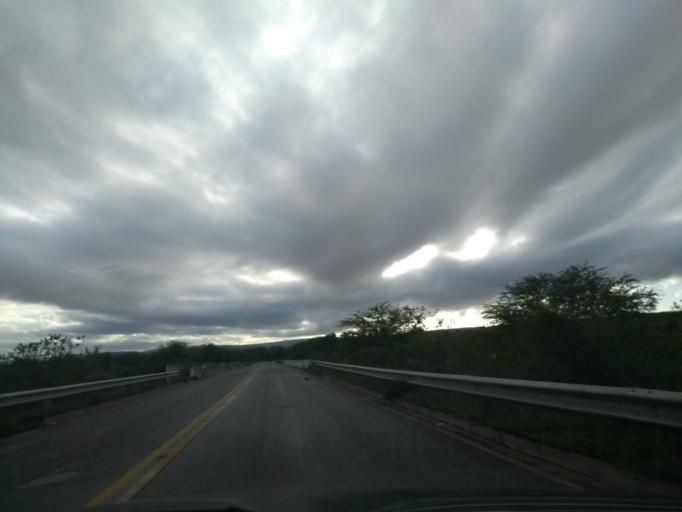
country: BR
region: Bahia
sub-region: Ituacu
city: Ituacu
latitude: -13.7685
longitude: -41.0432
